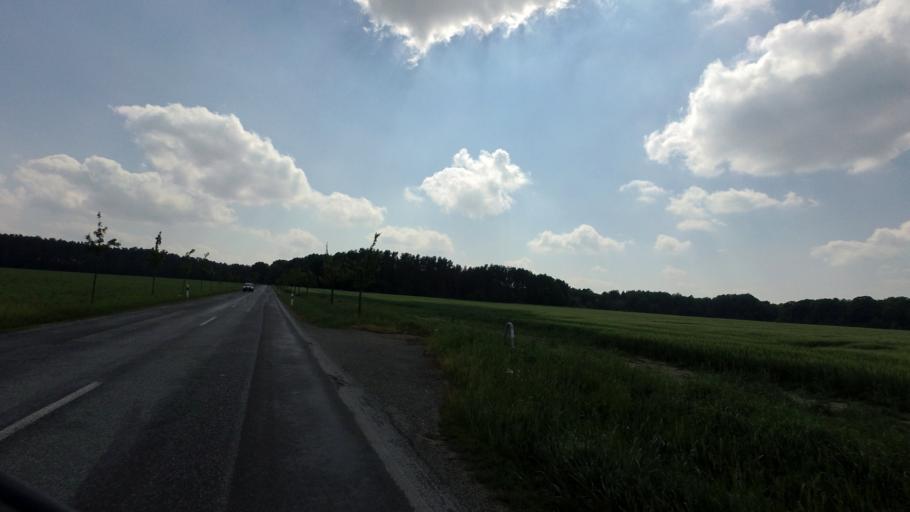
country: DE
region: Saxony
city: Mucka
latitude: 51.2898
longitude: 14.6597
